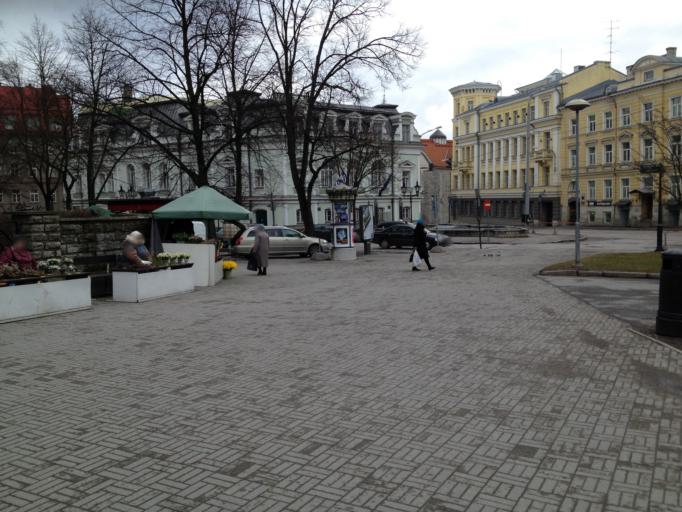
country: EE
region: Harju
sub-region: Tallinna linn
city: Tallinn
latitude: 59.4342
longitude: 24.7460
